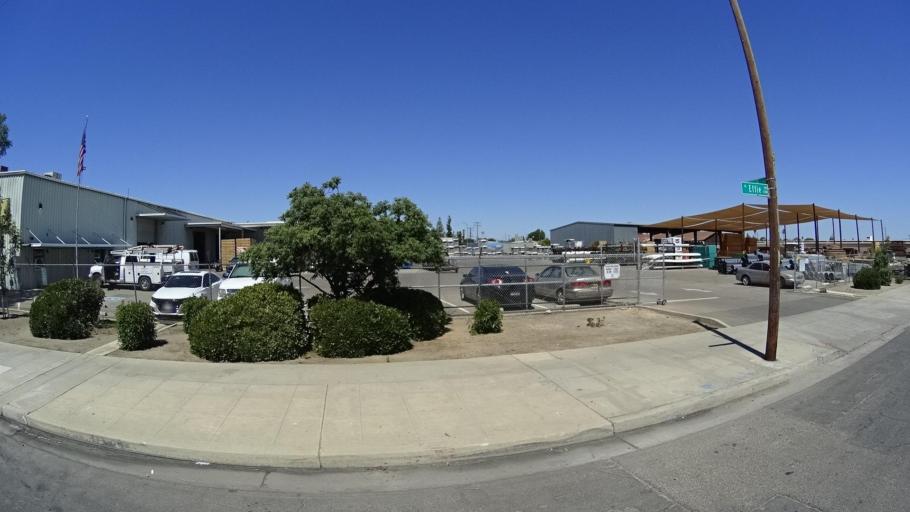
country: US
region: California
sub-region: Fresno County
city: Fresno
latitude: 36.7967
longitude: -119.7883
